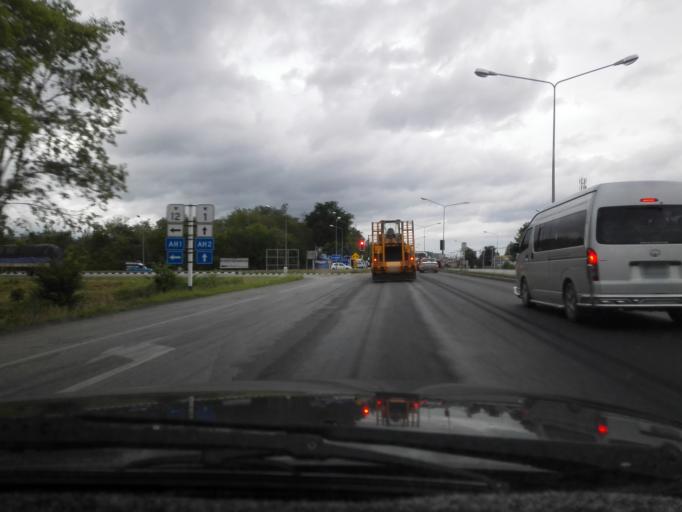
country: TH
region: Tak
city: Tak
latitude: 16.8408
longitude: 99.1141
